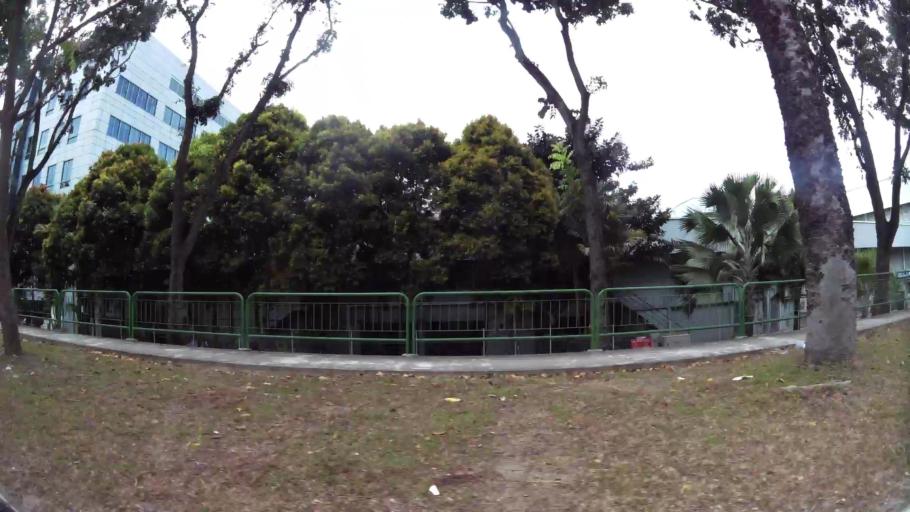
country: SG
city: Singapore
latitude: 1.3250
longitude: 103.7092
